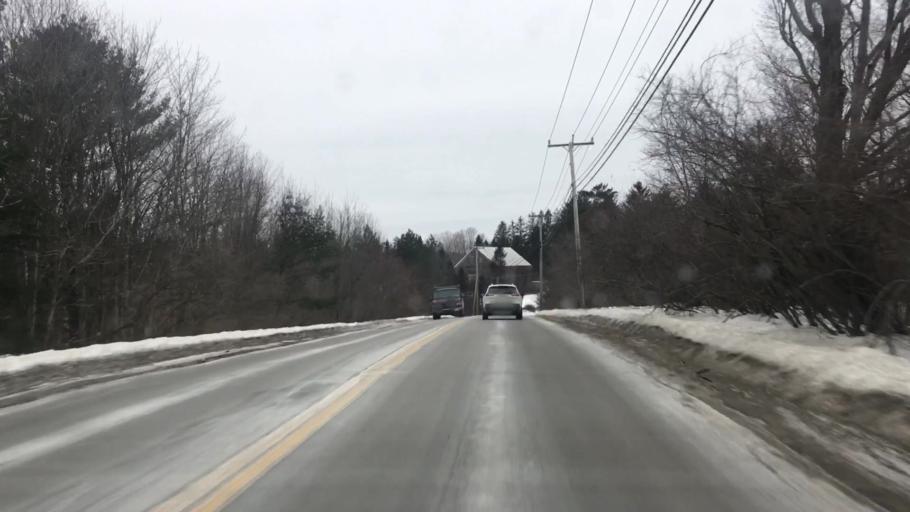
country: US
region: Maine
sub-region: Androscoggin County
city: Auburn
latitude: 44.1225
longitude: -70.2573
